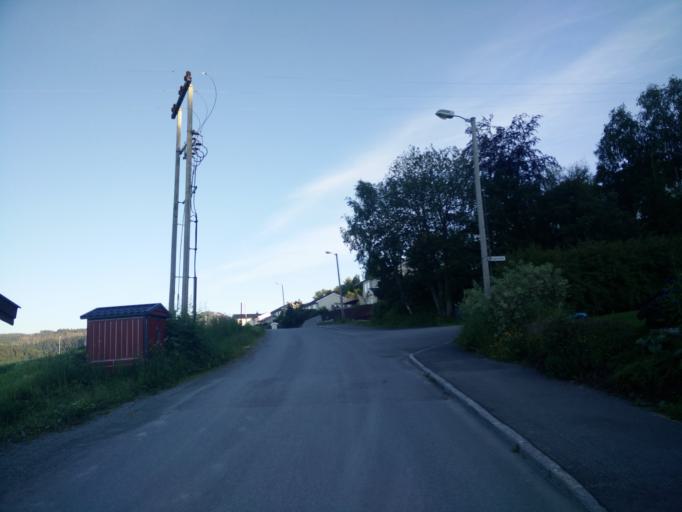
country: NO
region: Sor-Trondelag
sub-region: Skaun
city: Borsa
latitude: 63.3326
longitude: 10.0605
